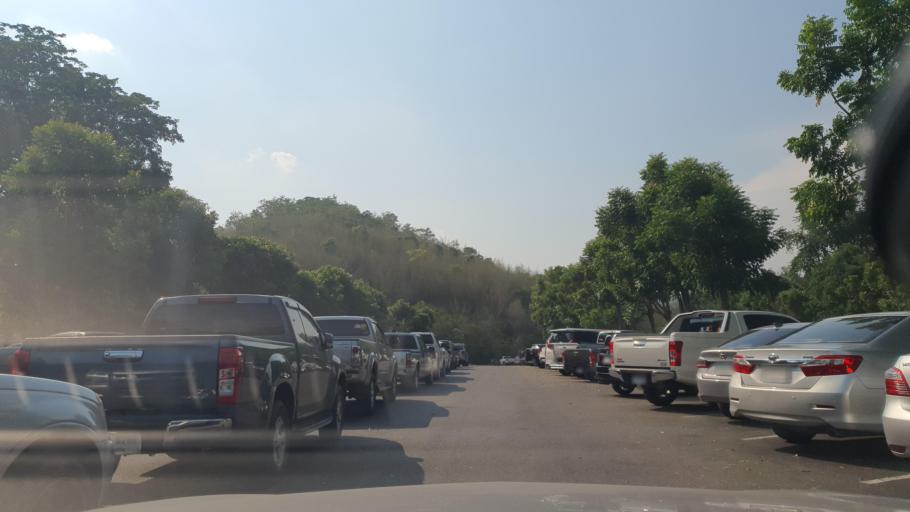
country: TH
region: Kanchanaburi
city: Si Sawat
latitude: 14.3753
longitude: 99.1440
